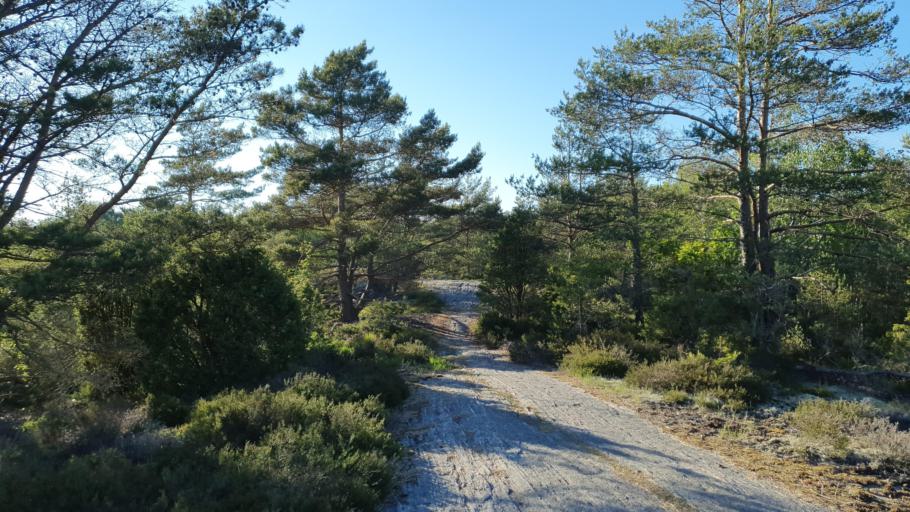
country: SE
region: Vaestra Goetaland
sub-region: Molndal
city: Kallered
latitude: 57.6305
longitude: 12.0621
